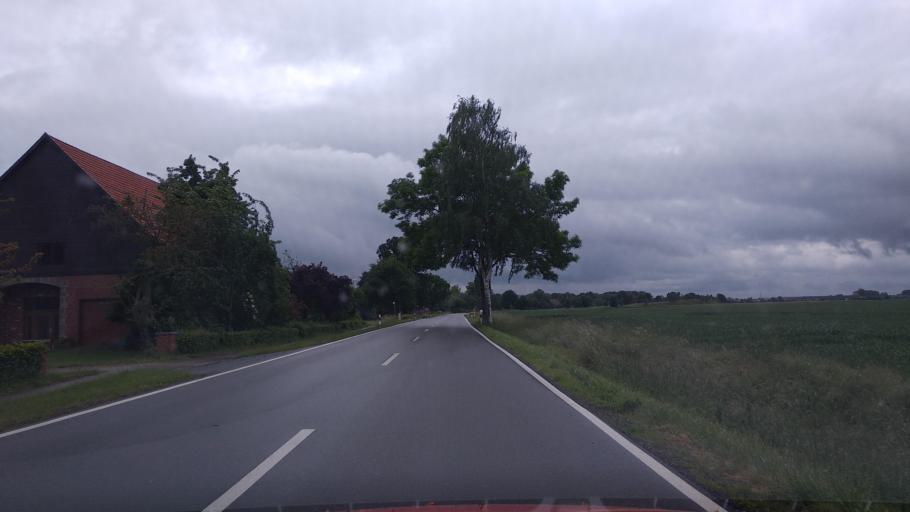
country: DE
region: Lower Saxony
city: Ludersfeld
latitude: 52.3482
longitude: 9.2393
